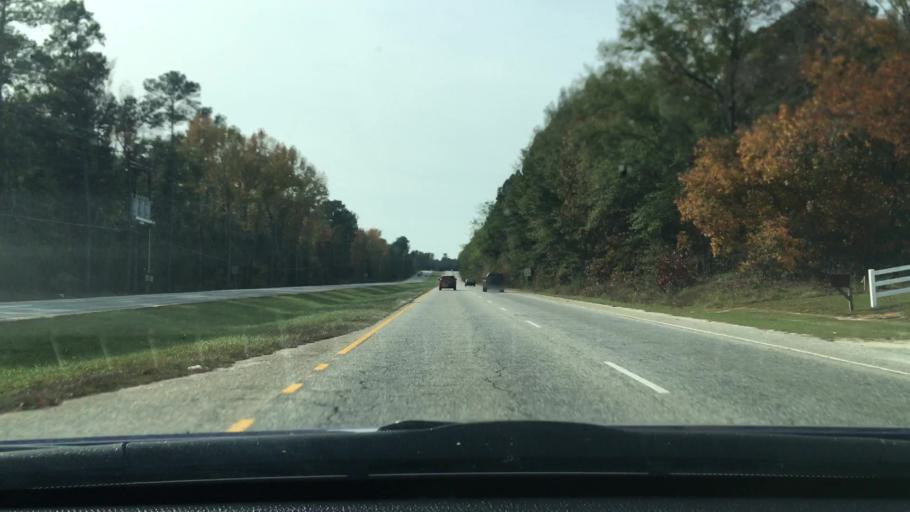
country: US
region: South Carolina
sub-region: Sumter County
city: Stateburg
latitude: 33.9481
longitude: -80.5052
